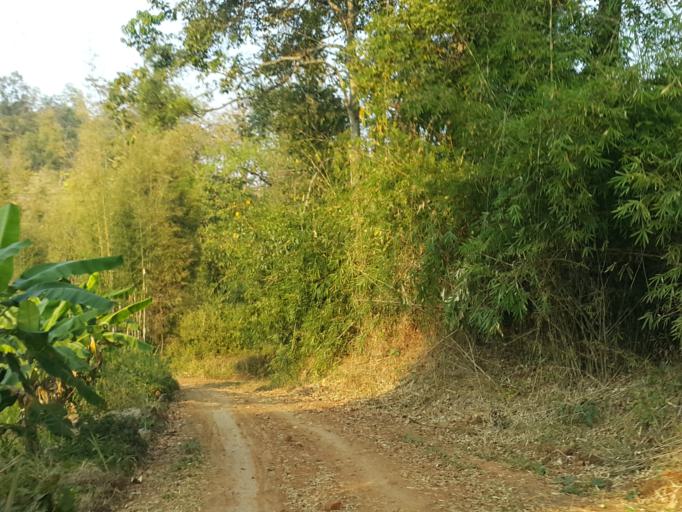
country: TH
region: Chiang Mai
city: Mae Taeng
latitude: 19.0555
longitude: 98.7665
